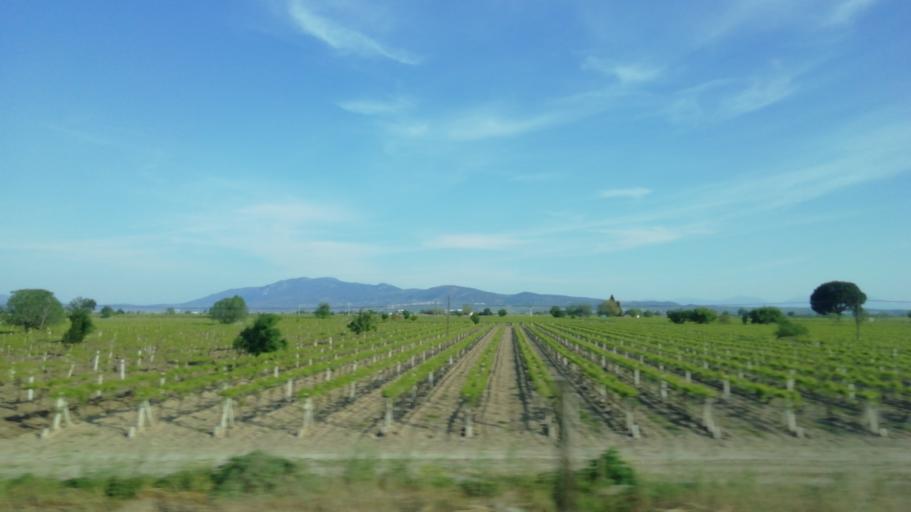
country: TR
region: Manisa
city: Saruhanli
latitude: 38.7493
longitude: 27.6203
